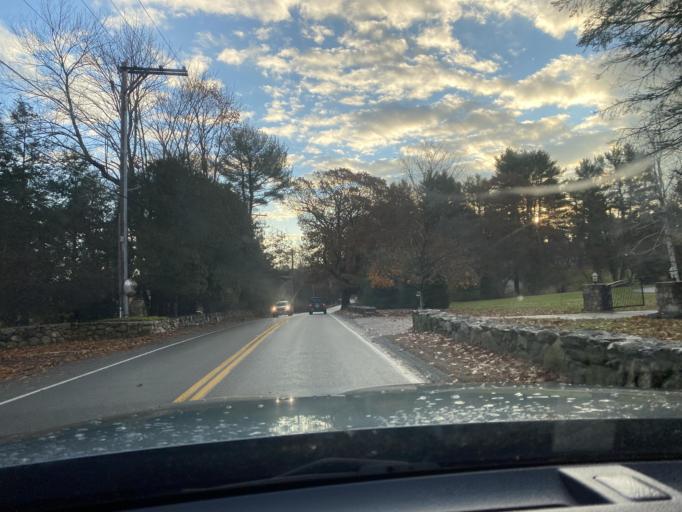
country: US
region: Massachusetts
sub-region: Norfolk County
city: Dover
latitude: 42.2535
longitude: -71.2556
